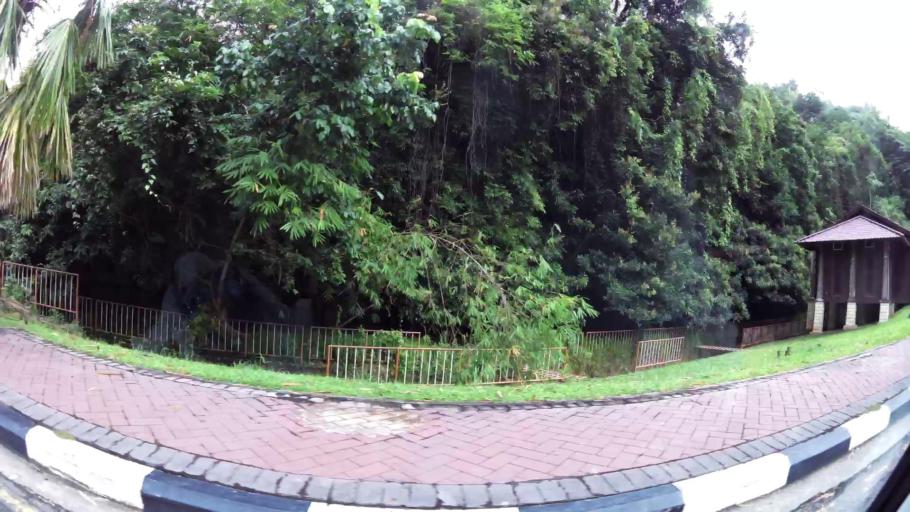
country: BN
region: Brunei and Muara
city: Bandar Seri Begawan
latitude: 4.9000
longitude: 114.9432
